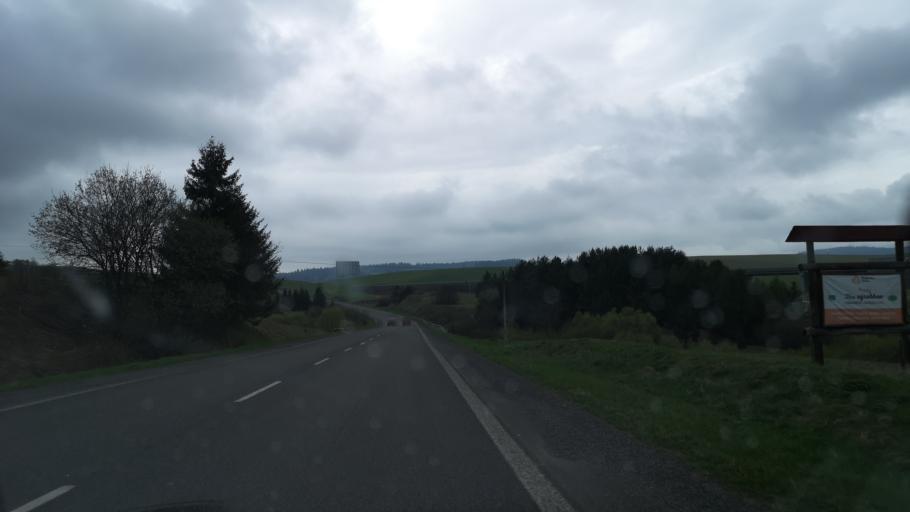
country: SK
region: Presovsky
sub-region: Okres Poprad
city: Strba
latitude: 49.0621
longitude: 19.9668
